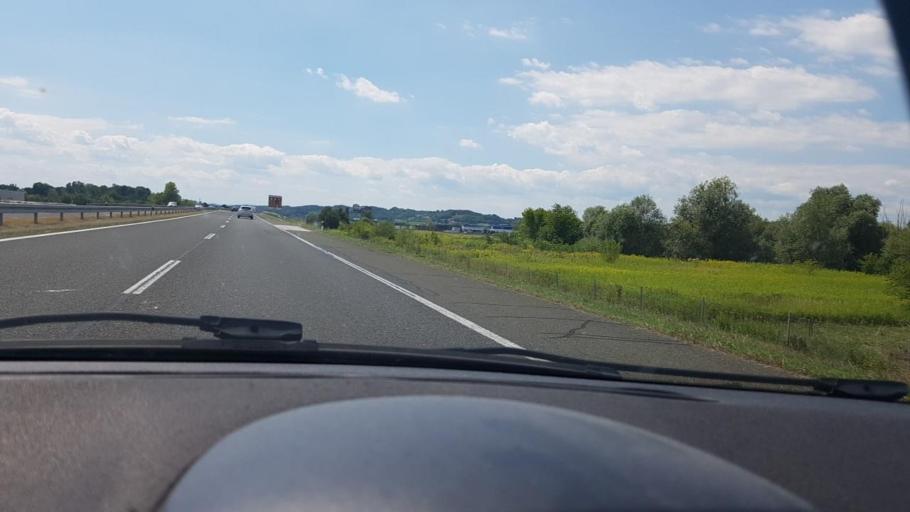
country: HR
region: Krapinsko-Zagorska
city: Oroslavje
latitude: 46.0097
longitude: 15.8826
